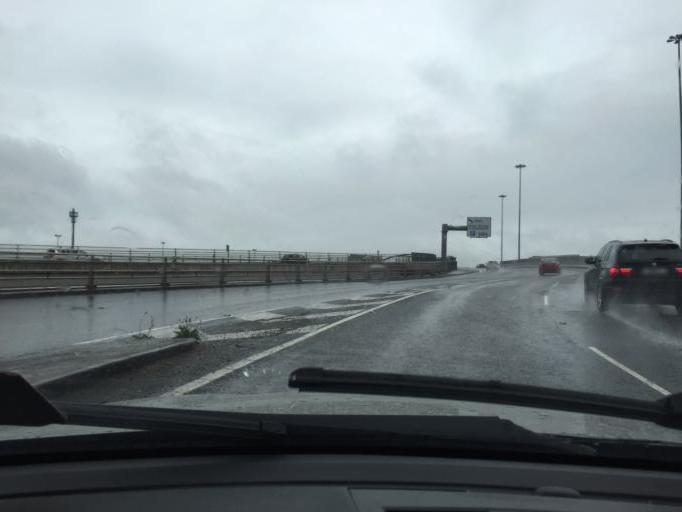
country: IE
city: Cherry Orchard
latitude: 53.3177
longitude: -6.3682
